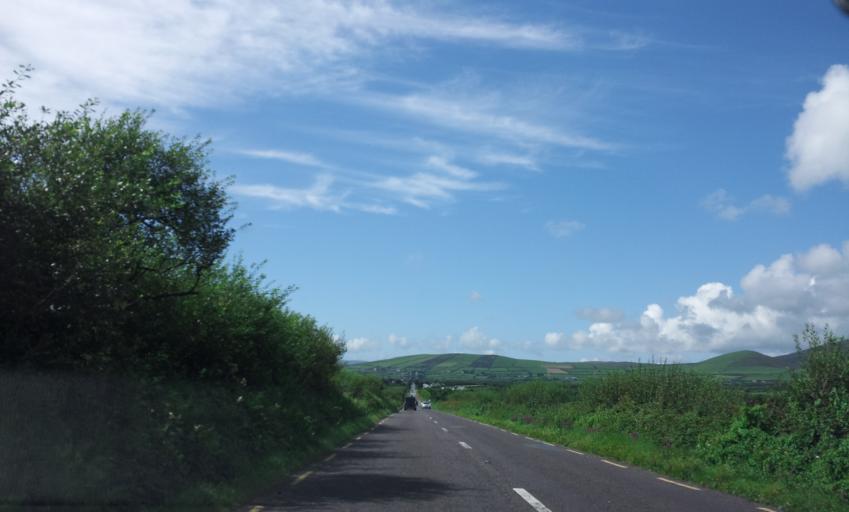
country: IE
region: Munster
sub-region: Ciarrai
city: Dingle
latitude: 52.1406
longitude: -10.1833
